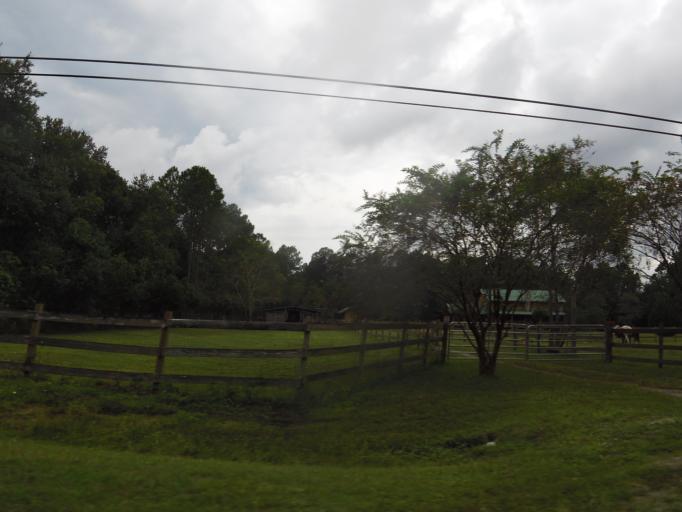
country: US
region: Florida
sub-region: Clay County
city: Middleburg
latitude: 30.1035
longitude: -81.9491
